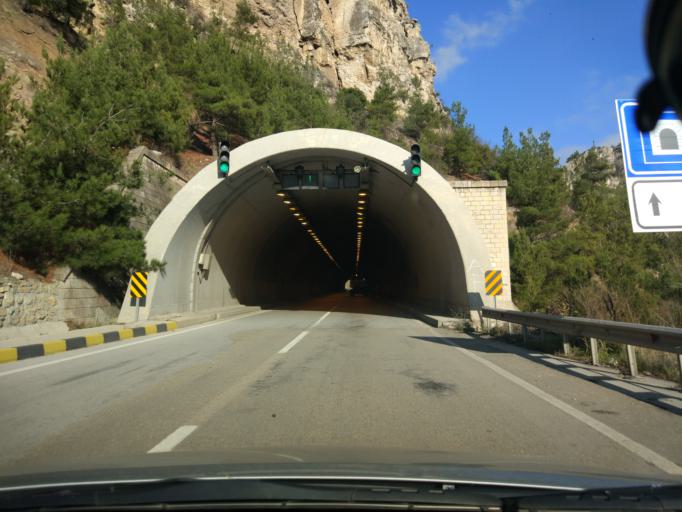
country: TR
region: Karabuk
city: Karabuk
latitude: 41.0797
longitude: 32.6698
